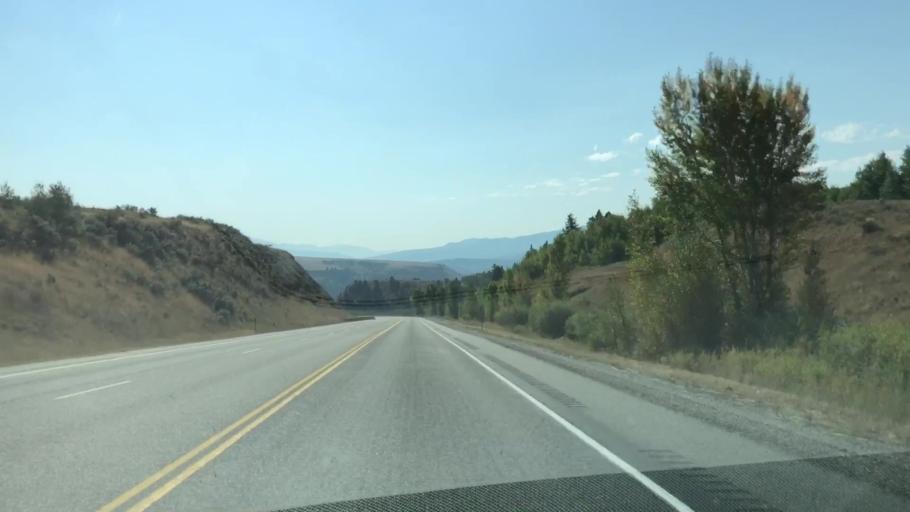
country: US
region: Idaho
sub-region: Teton County
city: Victor
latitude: 43.4916
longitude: -111.4536
